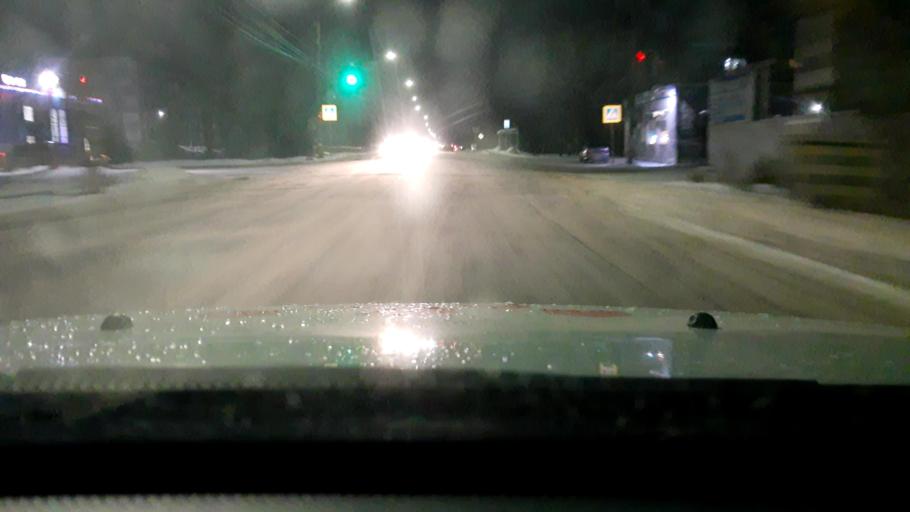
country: RU
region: Nizjnij Novgorod
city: Gorodets
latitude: 56.6704
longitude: 43.4668
